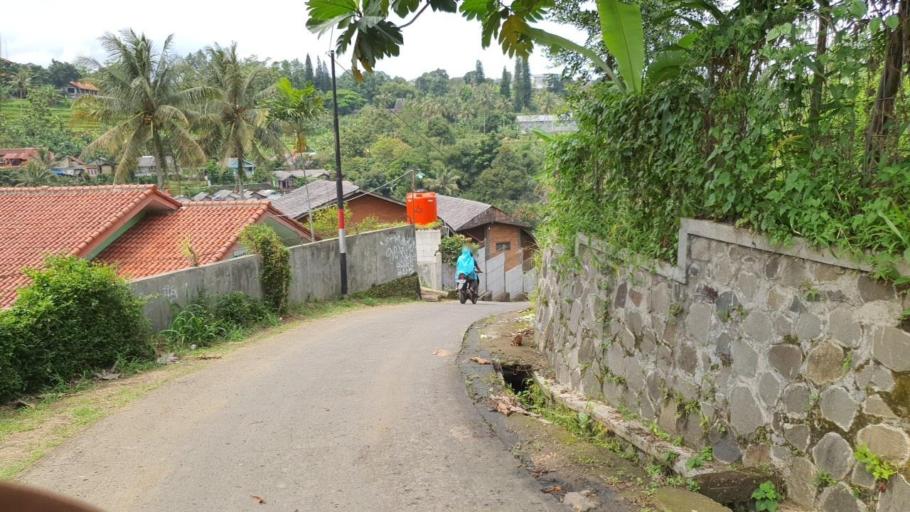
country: ID
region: West Java
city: Caringin
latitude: -6.6465
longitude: 106.8887
